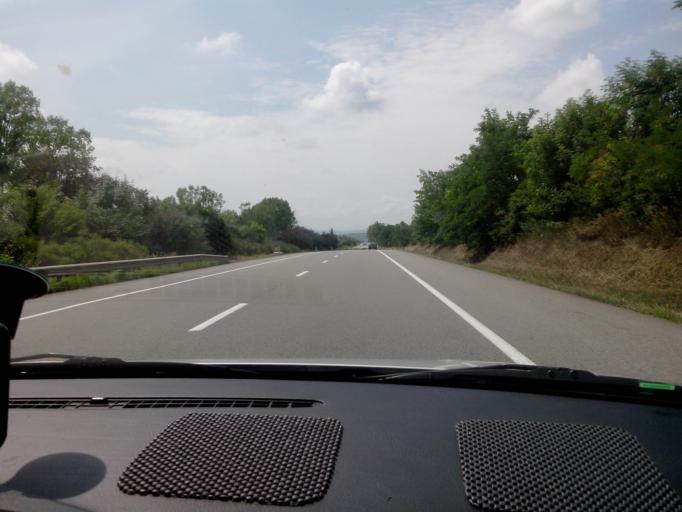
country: RO
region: Cluj
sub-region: Comuna Bontida
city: Rascruci
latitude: 46.8721
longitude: 23.7696
